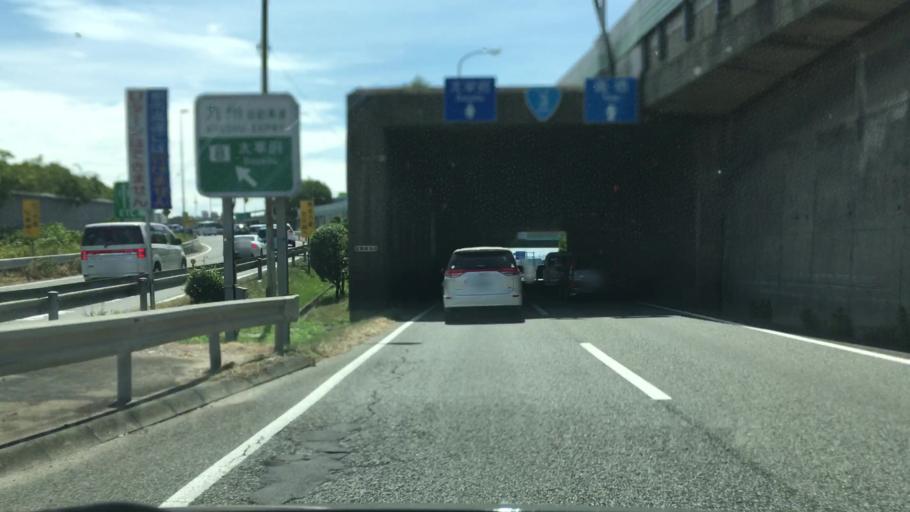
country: JP
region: Fukuoka
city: Onojo
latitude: 33.5325
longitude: 130.4908
